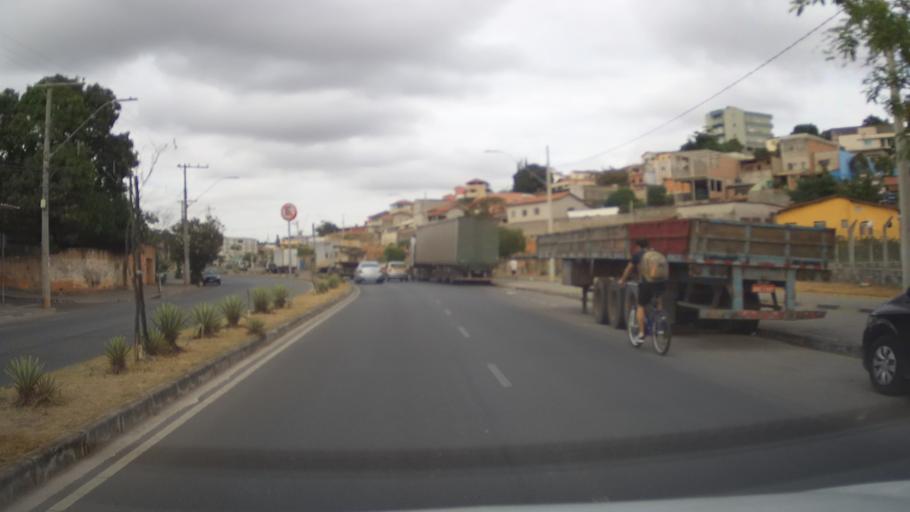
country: BR
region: Minas Gerais
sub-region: Belo Horizonte
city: Belo Horizonte
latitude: -19.8302
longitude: -43.9736
